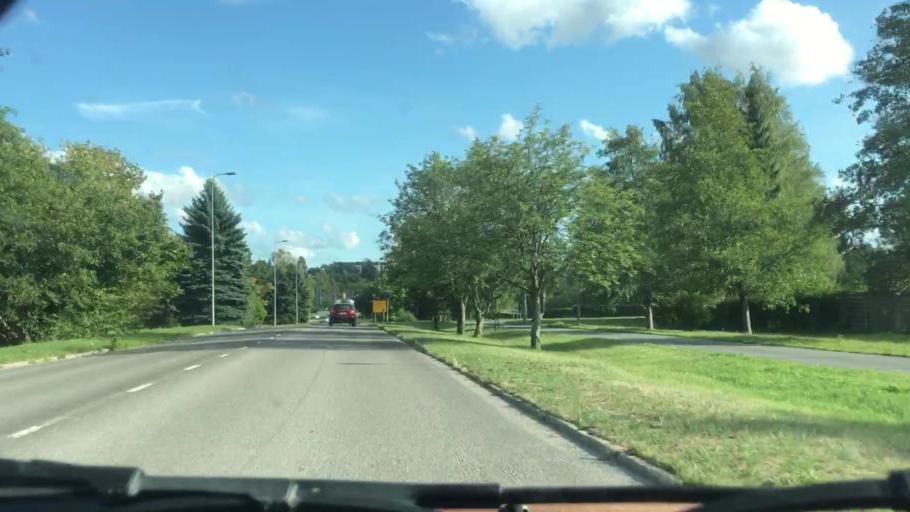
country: FI
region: Varsinais-Suomi
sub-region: Turku
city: Turku
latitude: 60.4629
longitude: 22.2432
